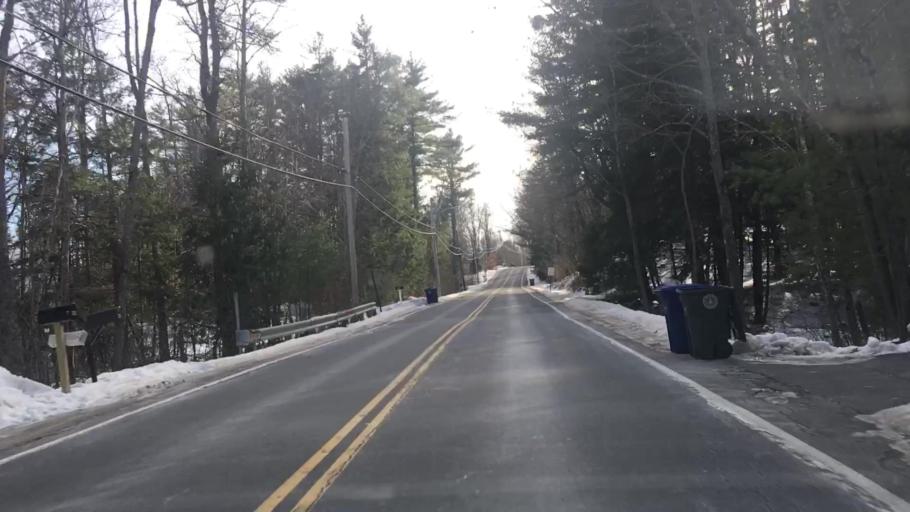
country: US
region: Maine
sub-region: Cumberland County
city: Westbrook
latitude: 43.7241
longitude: -70.3572
